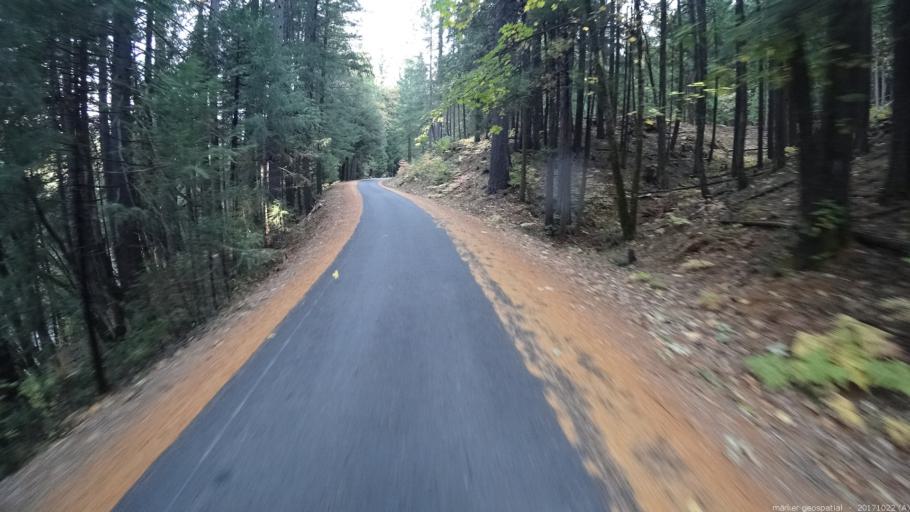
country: US
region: California
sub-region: Siskiyou County
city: Dunsmuir
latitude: 41.1537
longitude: -122.2894
